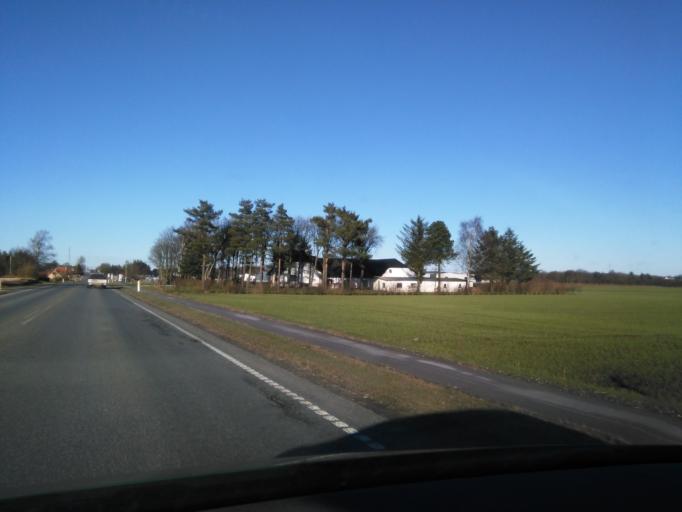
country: DK
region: North Denmark
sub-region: Mariagerfjord Kommune
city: Hobro
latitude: 56.6133
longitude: 9.8067
